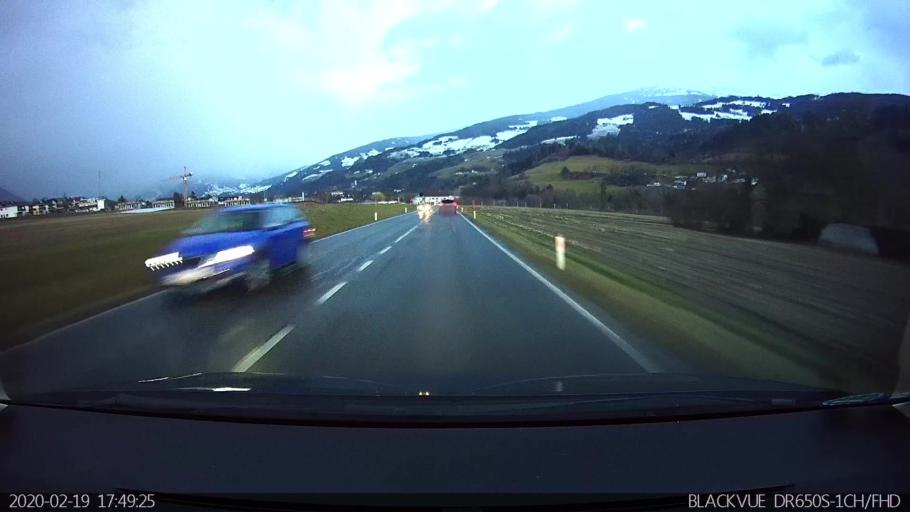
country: AT
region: Tyrol
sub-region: Politischer Bezirk Innsbruck Land
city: Hall in Tirol
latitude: 47.2805
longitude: 11.5214
